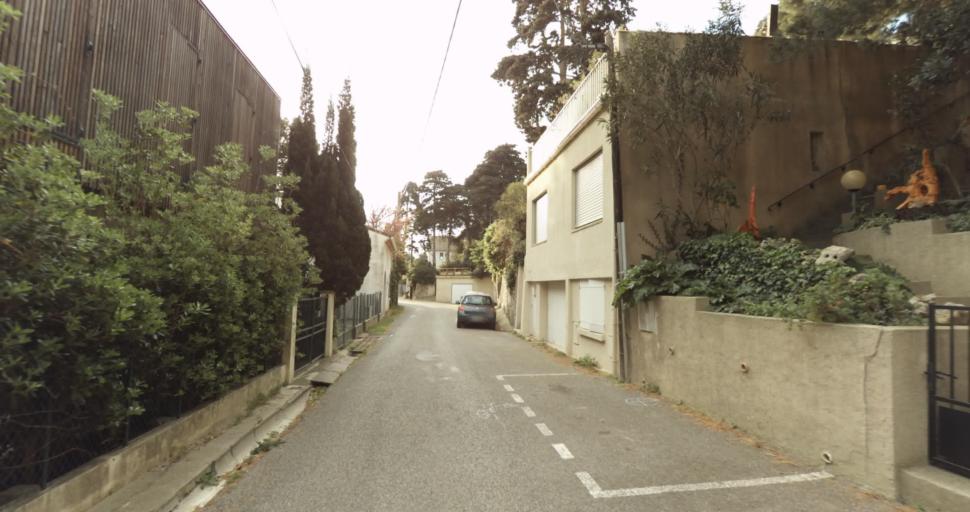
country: FR
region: Languedoc-Roussillon
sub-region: Departement de l'Aude
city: Leucate
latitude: 42.9316
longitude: 3.0352
